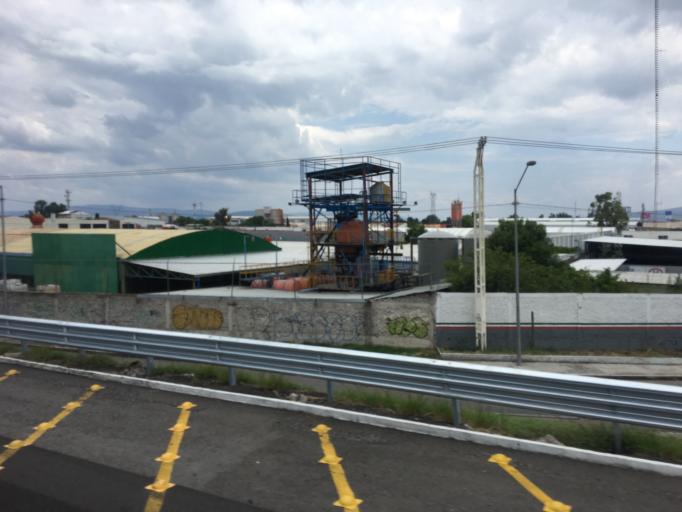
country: MX
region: Guanajuato
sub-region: Celaya
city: Roque
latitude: 20.5577
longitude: -100.8214
